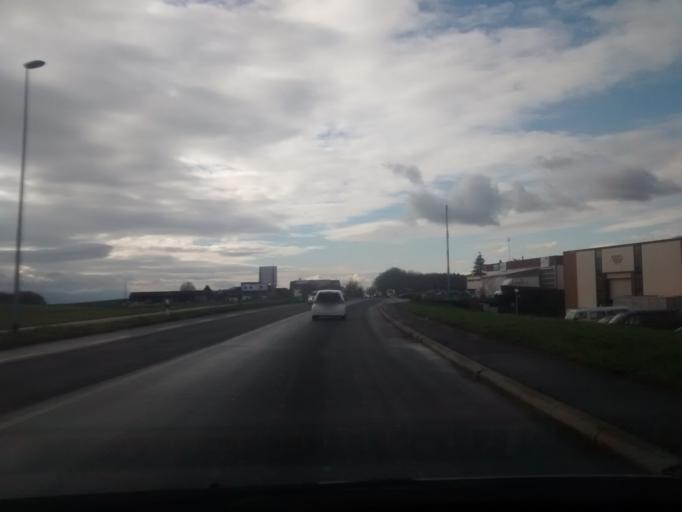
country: CH
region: Vaud
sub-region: Lausanne District
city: Cheseaux
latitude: 46.5775
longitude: 6.5914
